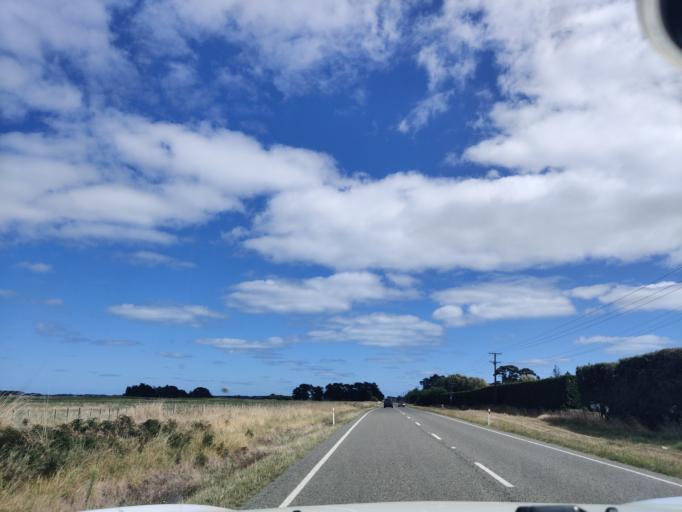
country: NZ
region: Manawatu-Wanganui
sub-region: Horowhenua District
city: Foxton
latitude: -40.3937
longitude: 175.3269
